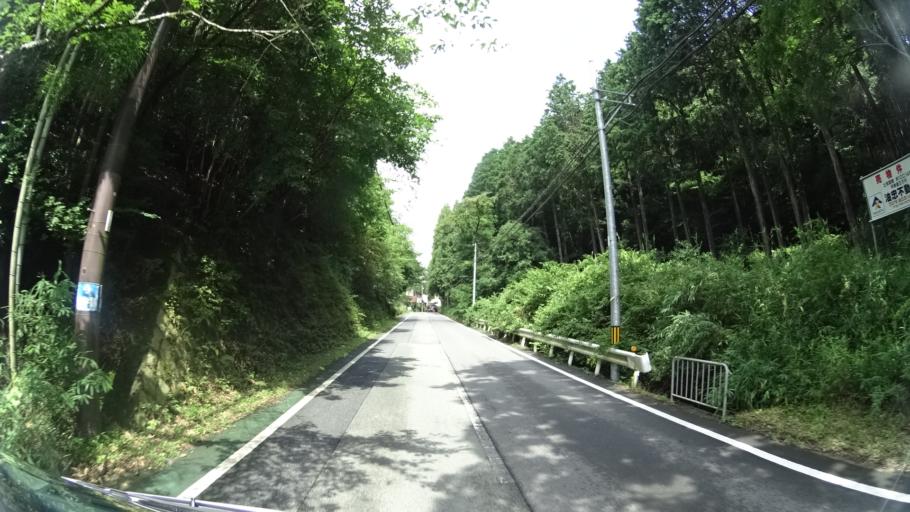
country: JP
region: Kyoto
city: Kameoka
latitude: 35.0191
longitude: 135.5168
